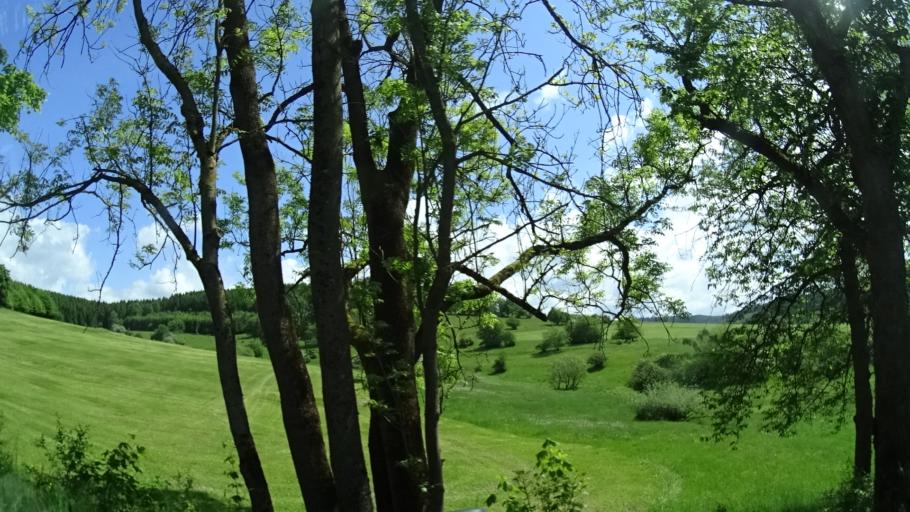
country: DE
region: Thuringia
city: Schmeheim
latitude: 50.5784
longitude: 10.5749
